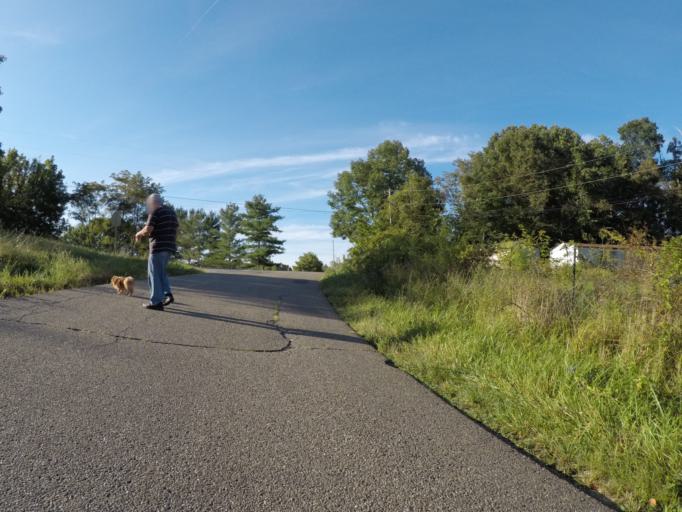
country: US
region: Ohio
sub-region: Lawrence County
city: Coal Grove
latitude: 38.5858
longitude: -82.5515
